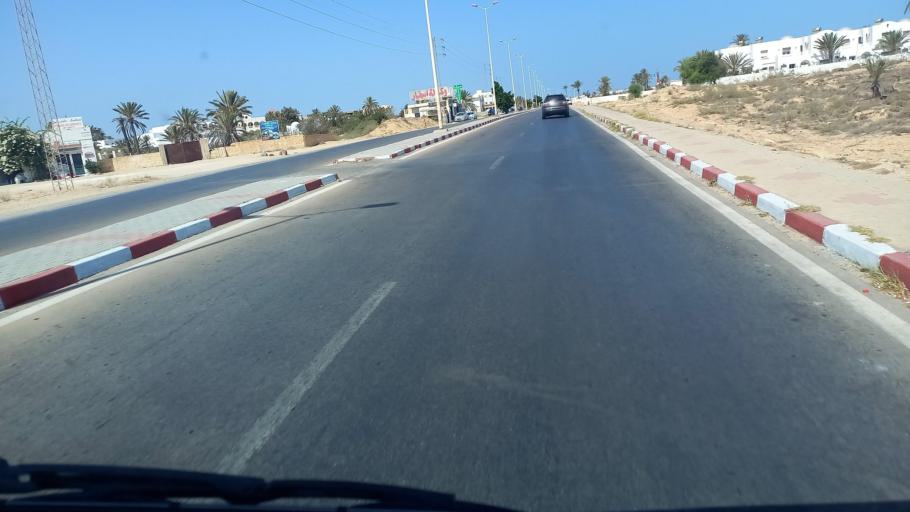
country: TN
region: Madanin
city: Midoun
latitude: 33.8607
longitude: 10.9697
